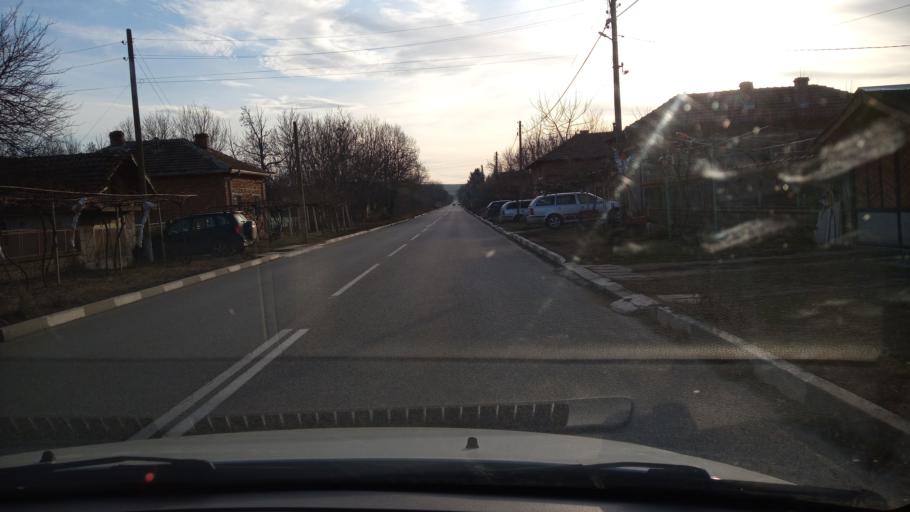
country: BG
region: Pleven
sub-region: Obshtina Pleven
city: Slavyanovo
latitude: 43.5604
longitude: 24.8687
